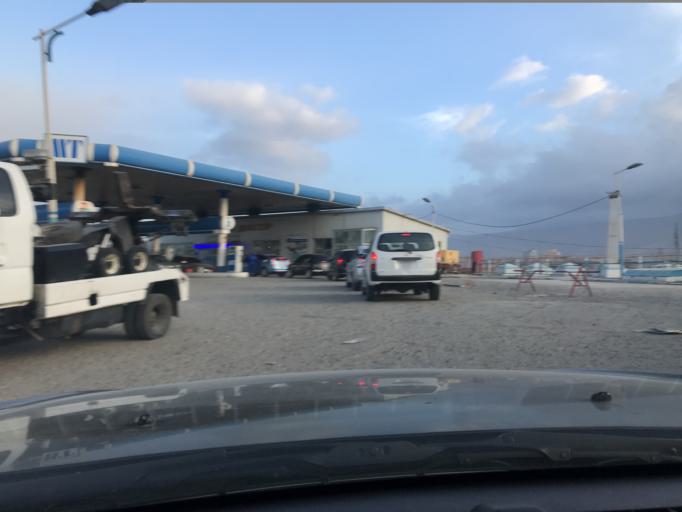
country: MN
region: Ulaanbaatar
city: Ulaanbaatar
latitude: 47.9240
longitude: 106.9951
